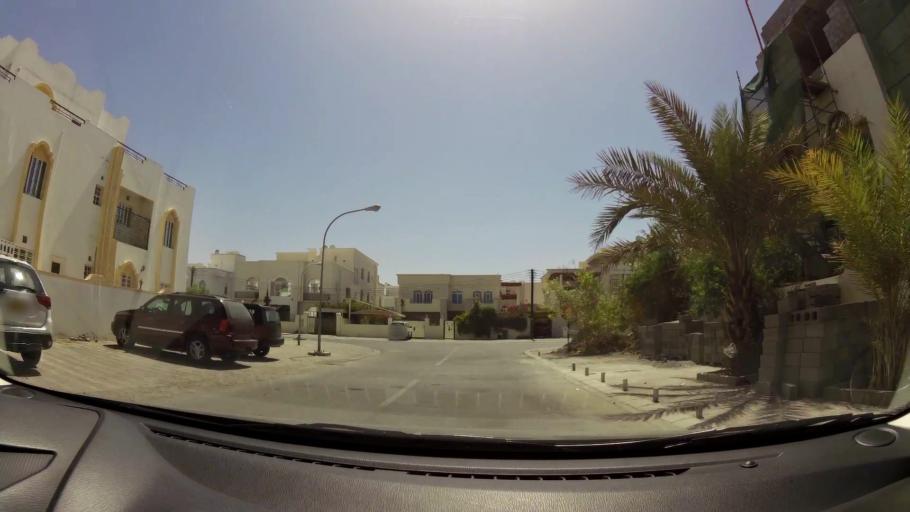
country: OM
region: Muhafazat Masqat
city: Bawshar
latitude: 23.5987
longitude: 58.3594
